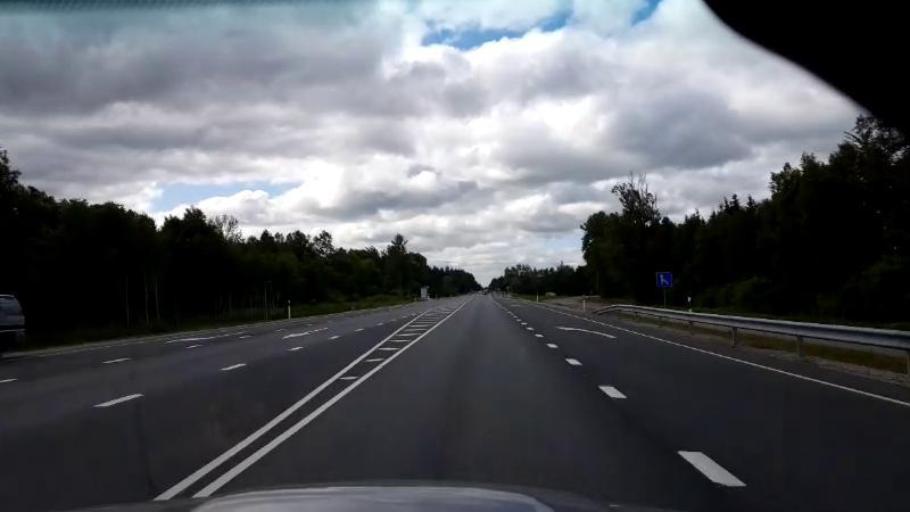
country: EE
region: Raplamaa
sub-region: Maerjamaa vald
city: Marjamaa
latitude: 58.8097
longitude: 24.4125
